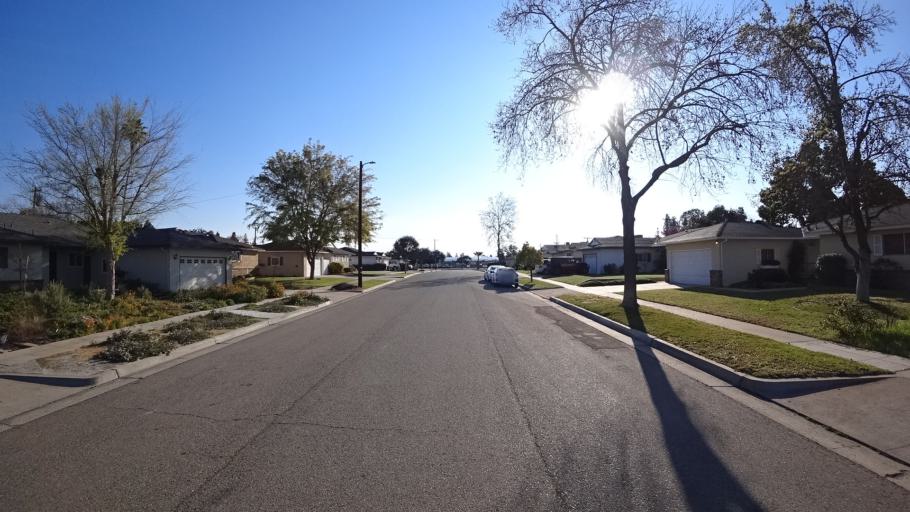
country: US
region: California
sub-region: Fresno County
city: Fresno
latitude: 36.8188
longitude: -119.7740
